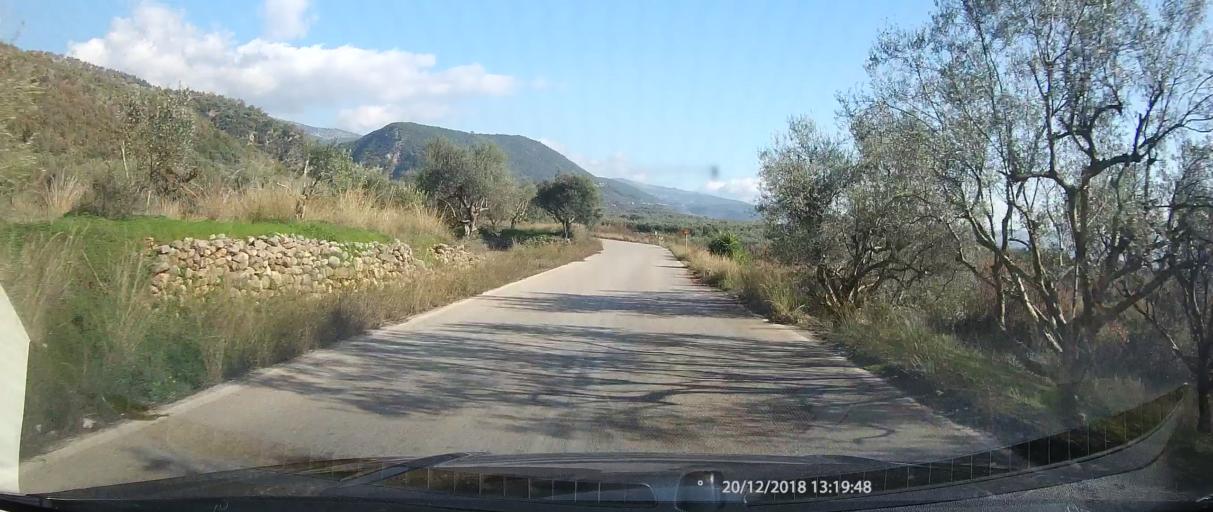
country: GR
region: West Greece
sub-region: Nomos Aitolias kai Akarnanias
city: Paravola
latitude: 38.6140
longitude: 21.5383
